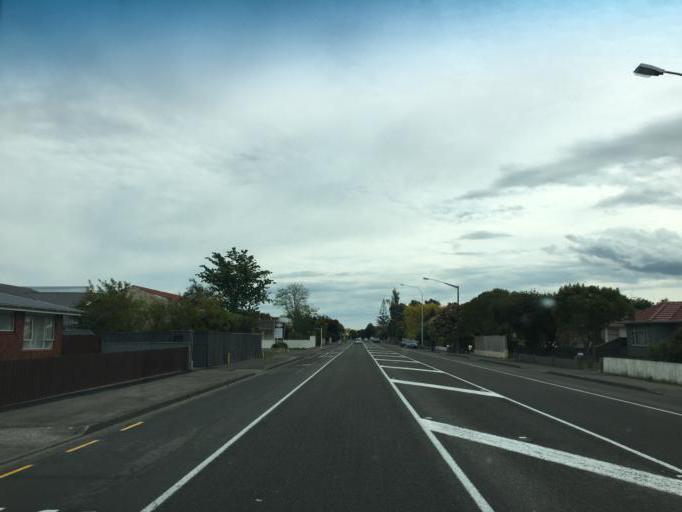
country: NZ
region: Manawatu-Wanganui
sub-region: Palmerston North City
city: Palmerston North
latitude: -40.3553
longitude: 175.5942
